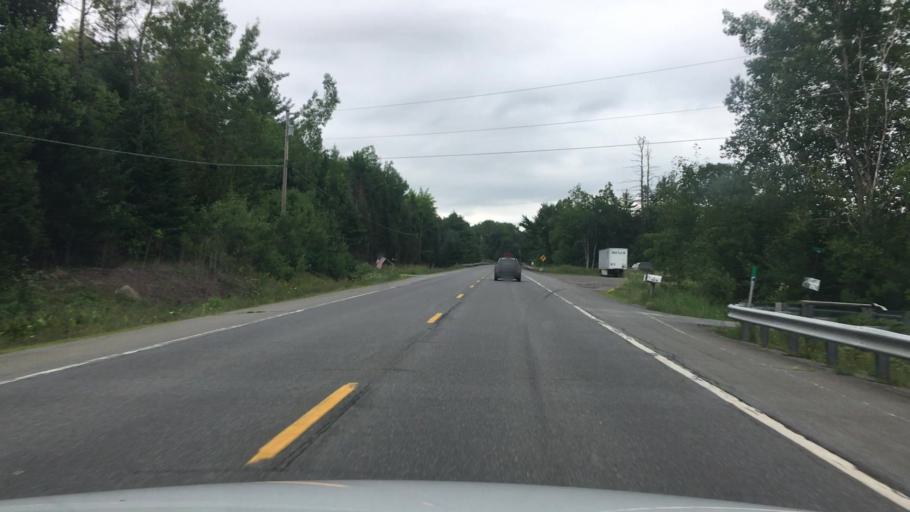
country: US
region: Maine
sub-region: Penobscot County
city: Bradley
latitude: 44.8257
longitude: -68.3958
